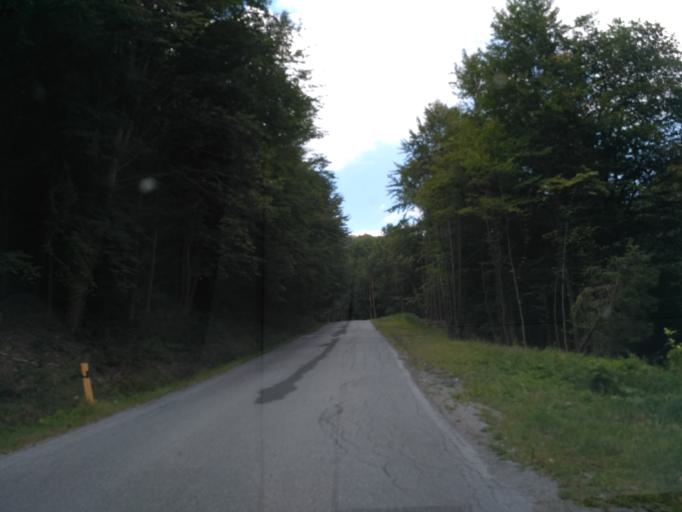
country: SK
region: Kosicky
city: Gelnica
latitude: 48.9199
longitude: 21.0367
